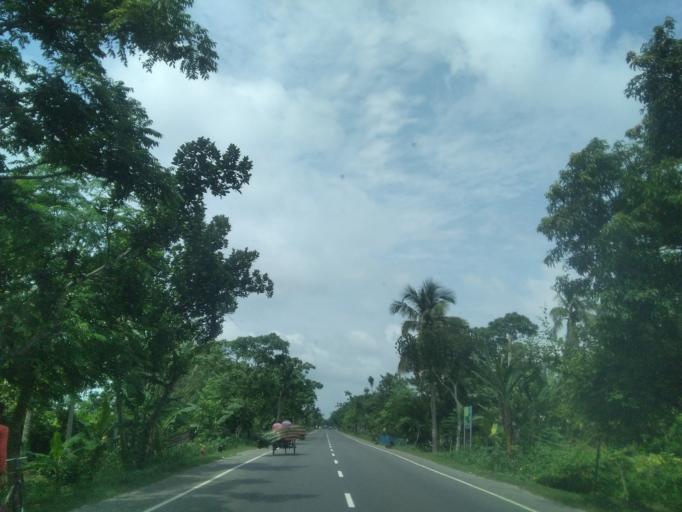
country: BD
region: Khulna
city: Kesabpur
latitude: 22.8042
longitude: 89.2358
